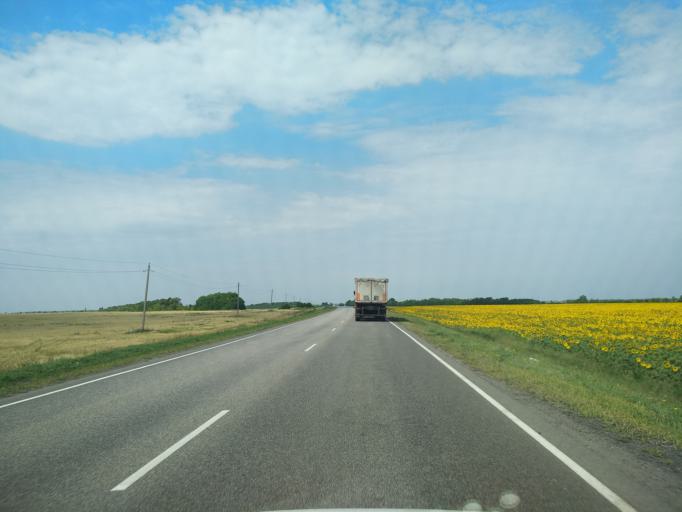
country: RU
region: Voronezj
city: Orlovo
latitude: 51.6783
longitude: 39.7858
